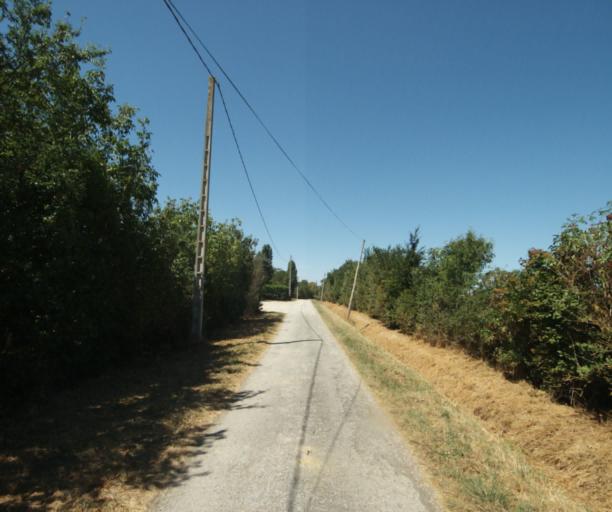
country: FR
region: Midi-Pyrenees
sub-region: Departement de la Haute-Garonne
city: Saint-Felix-Lauragais
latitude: 43.4708
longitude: 1.9419
